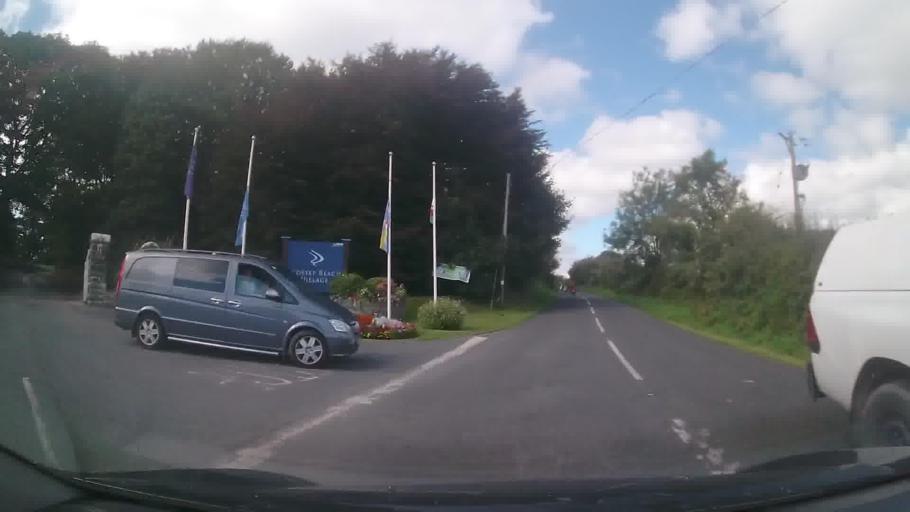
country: GB
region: Wales
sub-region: Pembrokeshire
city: Penally
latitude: 51.6564
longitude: -4.7563
